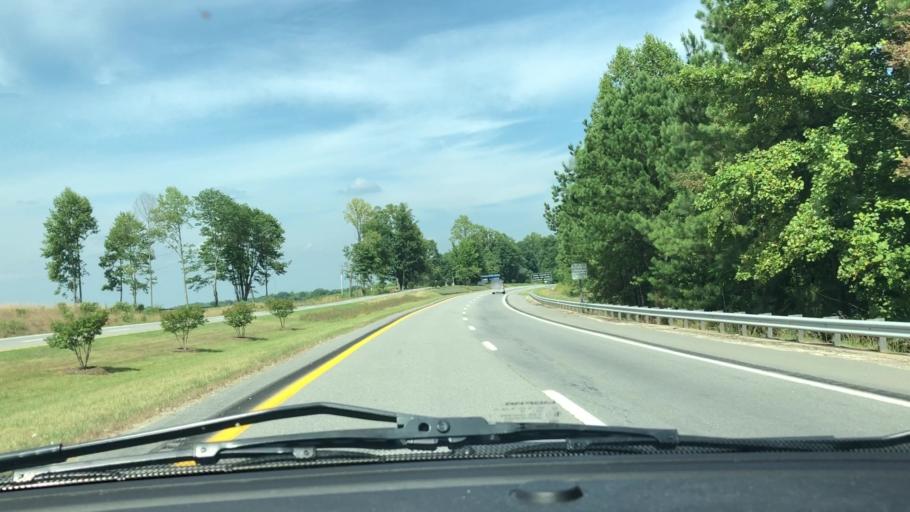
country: US
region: North Carolina
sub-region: Rockingham County
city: Stoneville
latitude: 36.5439
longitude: -79.9092
